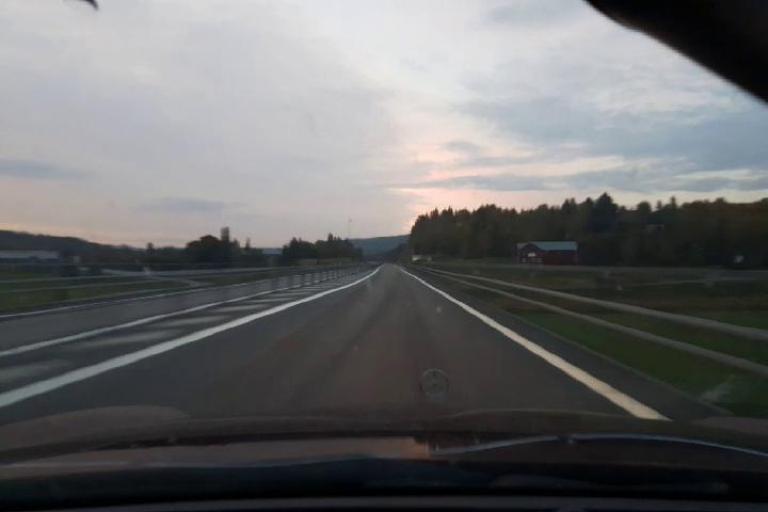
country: SE
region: Vaesternorrland
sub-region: Kramfors Kommun
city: Nordingra
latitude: 62.9287
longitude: 18.0974
